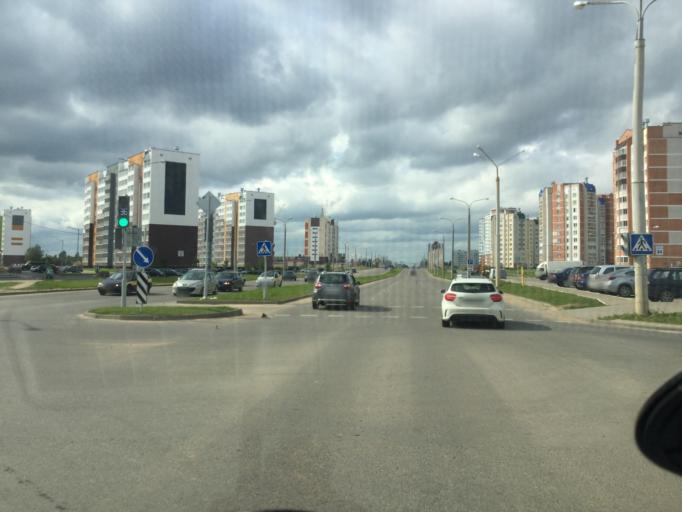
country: BY
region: Vitebsk
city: Vitebsk
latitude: 55.1639
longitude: 30.2761
